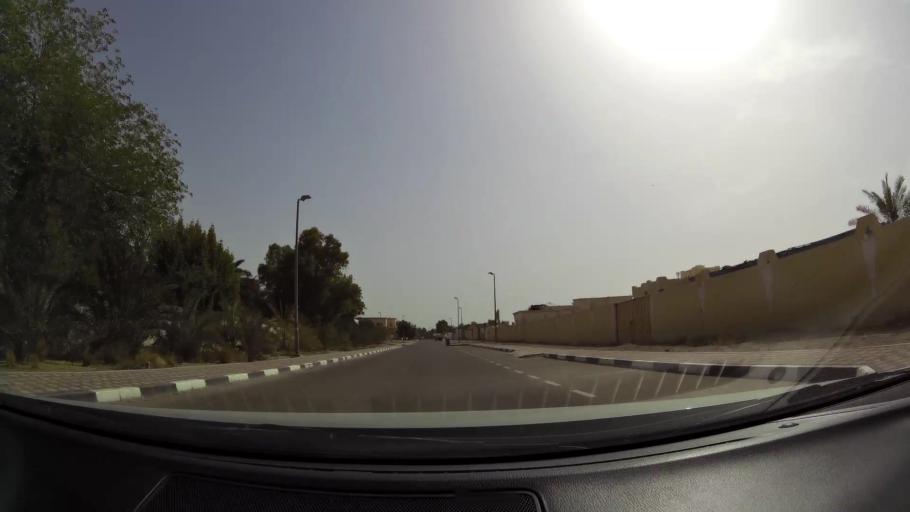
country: AE
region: Abu Dhabi
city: Al Ain
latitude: 24.1544
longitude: 55.7078
